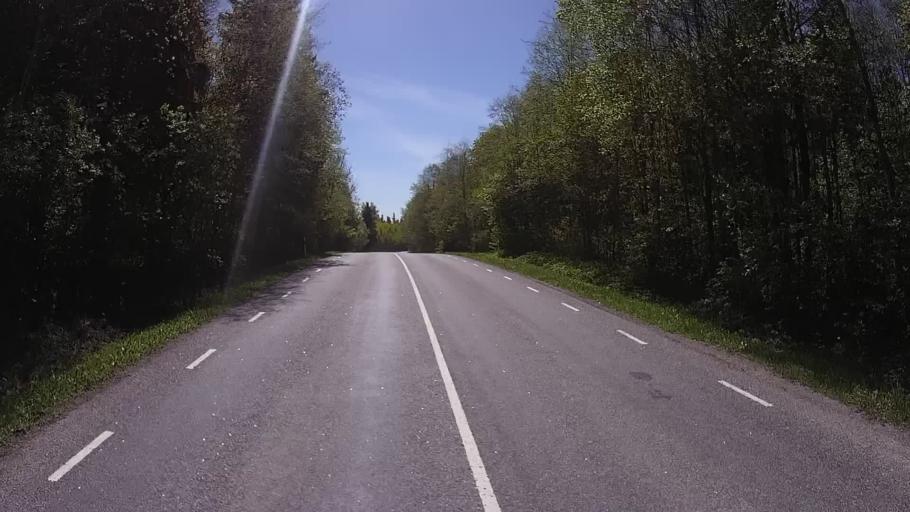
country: EE
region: Harju
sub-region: Rae vald
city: Vaida
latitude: 59.0588
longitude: 25.1396
